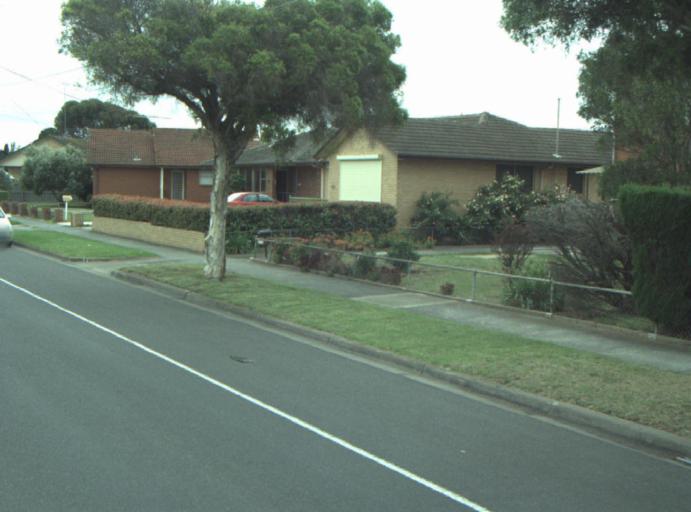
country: AU
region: Victoria
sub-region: Greater Geelong
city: Bell Park
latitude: -38.0782
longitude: 144.3474
